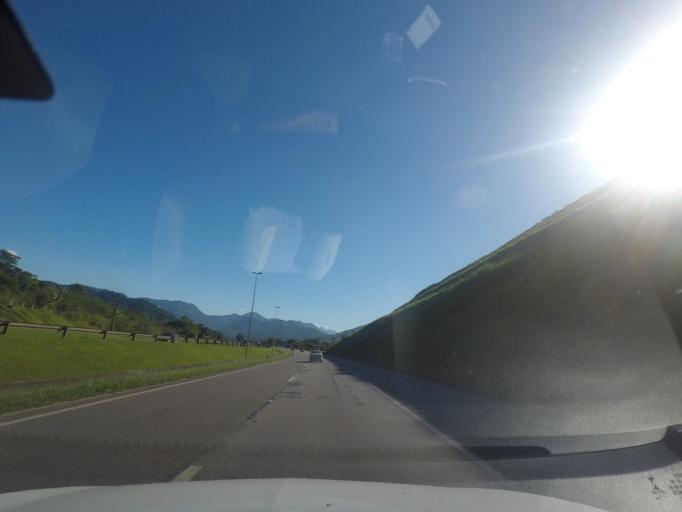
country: BR
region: Rio de Janeiro
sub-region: Guapimirim
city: Guapimirim
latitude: -22.5683
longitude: -43.0028
